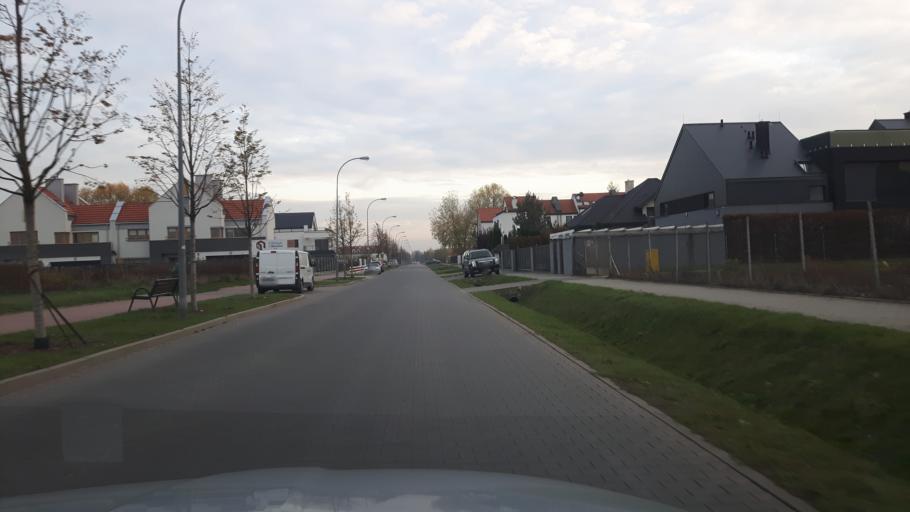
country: PL
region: Masovian Voivodeship
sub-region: Warszawa
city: Wilanow
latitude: 52.1803
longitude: 21.1064
